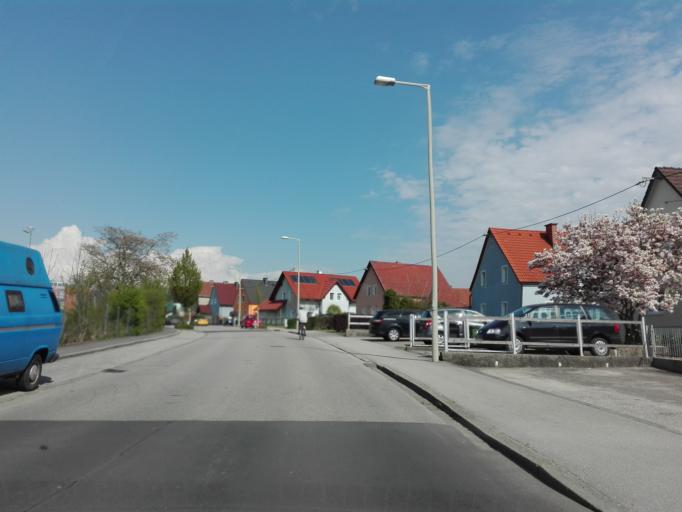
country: AT
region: Upper Austria
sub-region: Politischer Bezirk Linz-Land
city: Ansfelden
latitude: 48.2478
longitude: 14.2911
